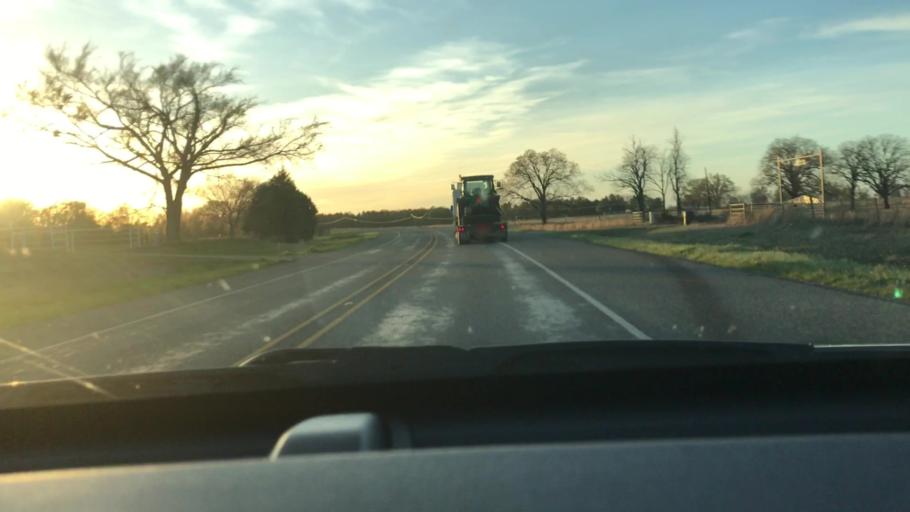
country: US
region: Texas
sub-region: Lamar County
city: Blossom
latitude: 33.6639
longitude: -95.3122
